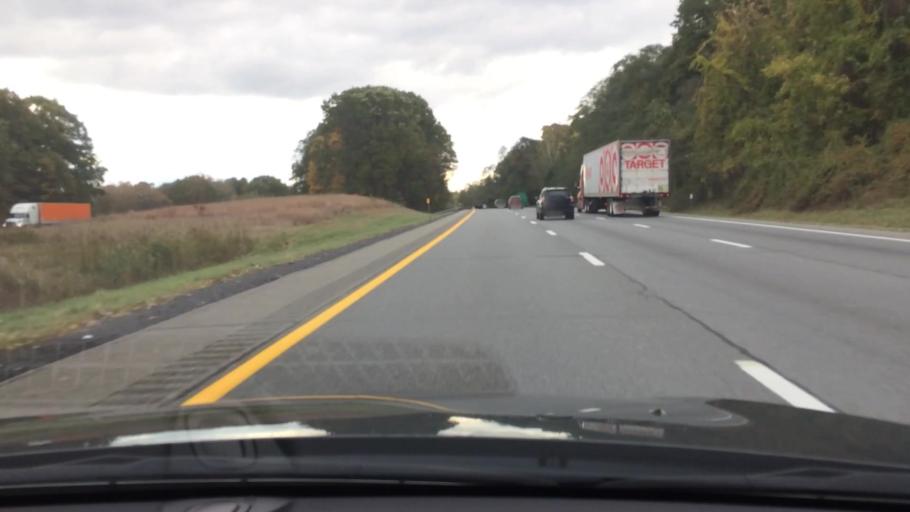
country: US
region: New York
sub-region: Saratoga County
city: Country Knolls
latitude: 42.9244
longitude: -73.8022
